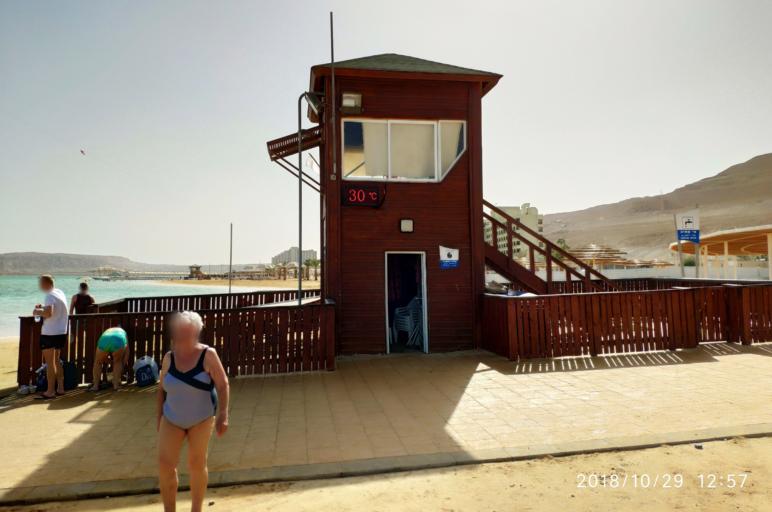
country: IL
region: Southern District
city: `En Boqeq
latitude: 31.1742
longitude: 35.3693
